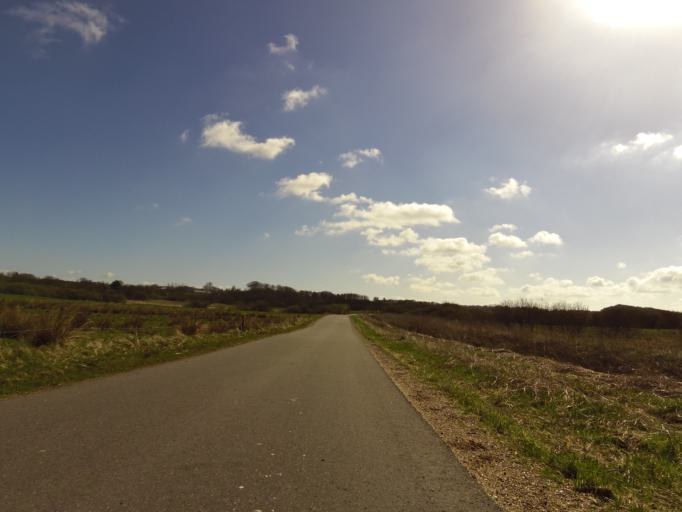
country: DK
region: Central Jutland
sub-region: Holstebro Kommune
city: Vinderup
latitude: 56.4273
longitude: 8.7352
